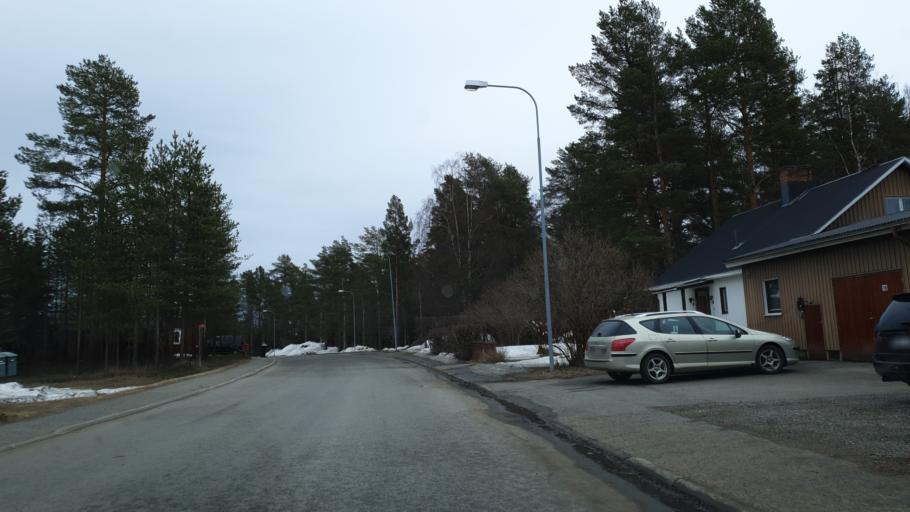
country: SE
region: Vaesterbotten
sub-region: Skelleftea Kommun
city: Byske
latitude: 64.9503
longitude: 21.2098
